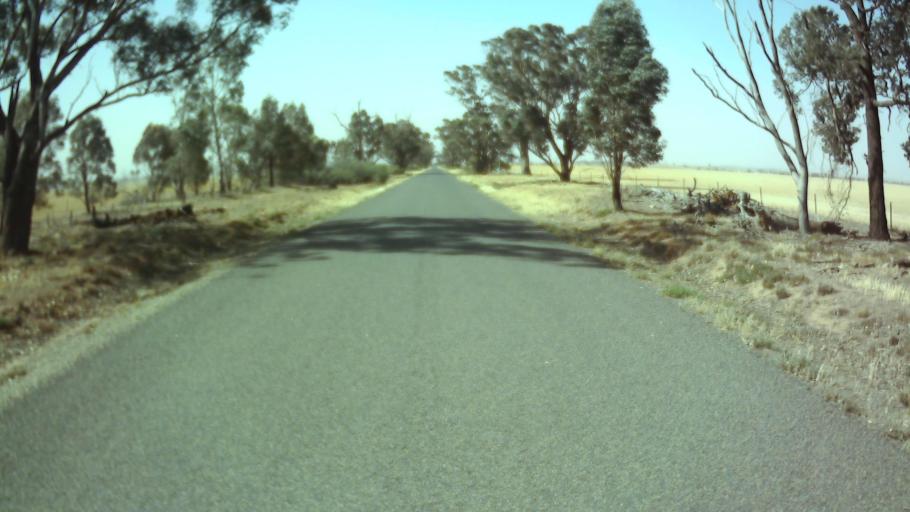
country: AU
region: New South Wales
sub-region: Weddin
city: Grenfell
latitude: -33.8909
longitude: 147.9226
